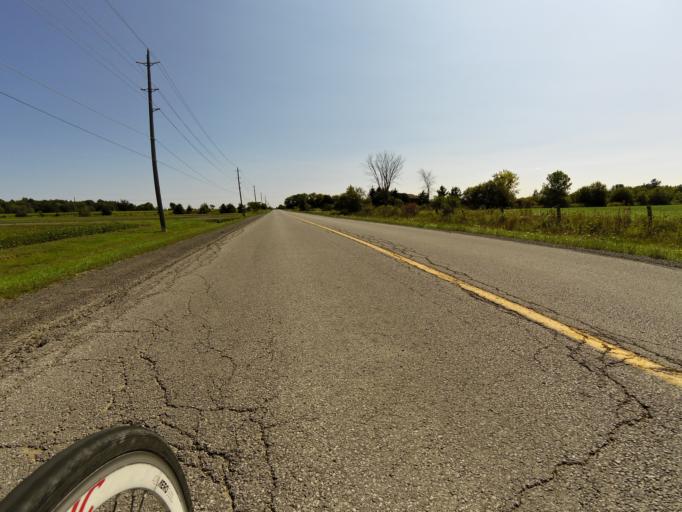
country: CA
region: Ontario
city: Arnprior
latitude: 45.4677
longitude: -76.1062
